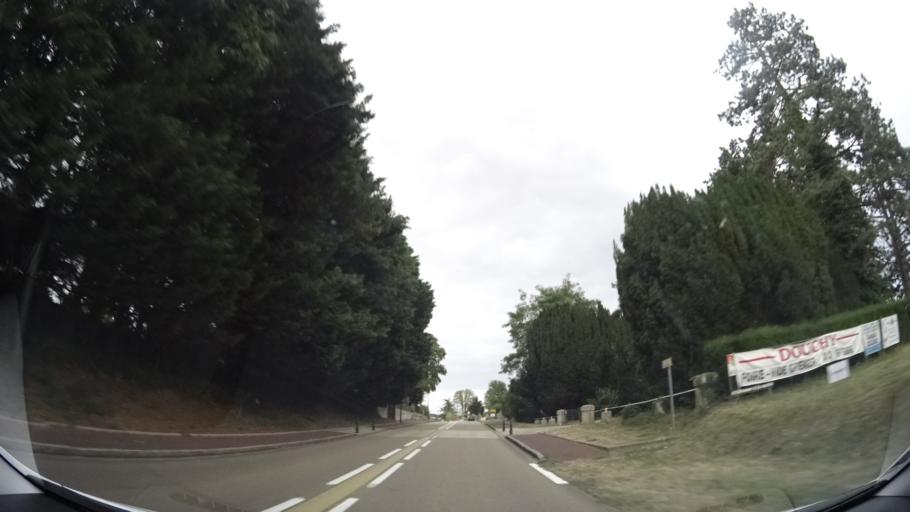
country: FR
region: Centre
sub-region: Departement du Loiret
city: Douchy
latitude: 47.9445
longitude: 3.0445
